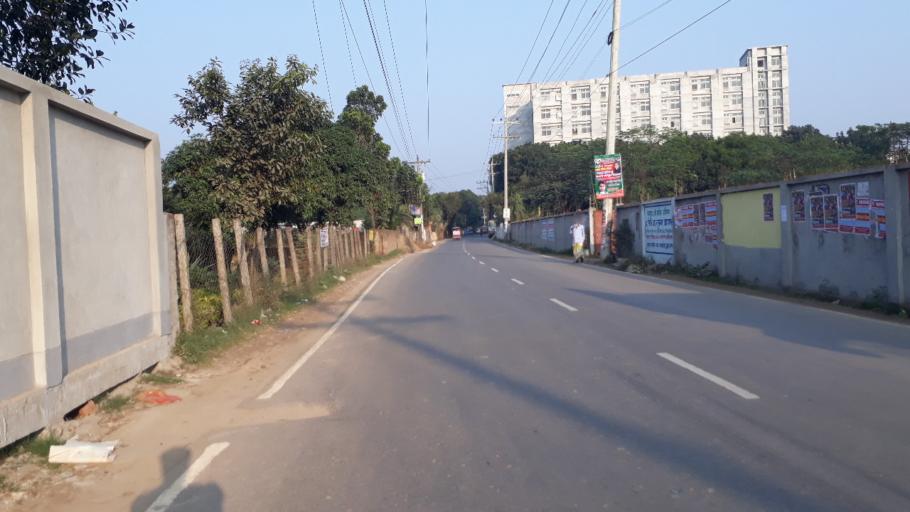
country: BD
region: Dhaka
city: Tungi
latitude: 23.8844
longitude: 90.3052
